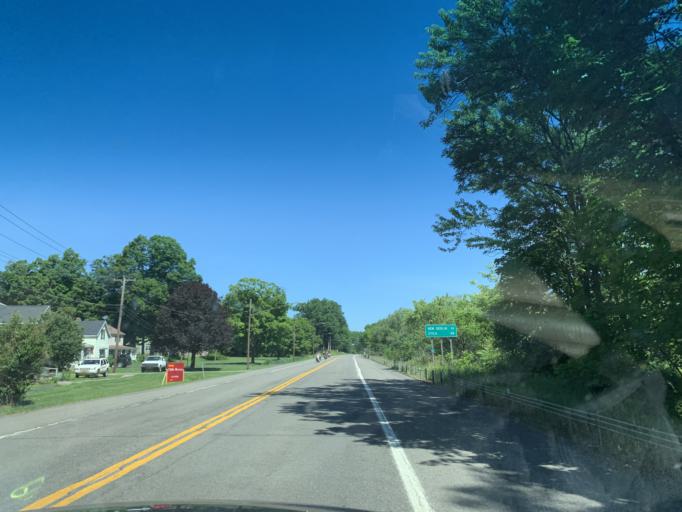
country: US
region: New York
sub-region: Delaware County
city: Sidney
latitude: 42.4313
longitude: -75.3853
